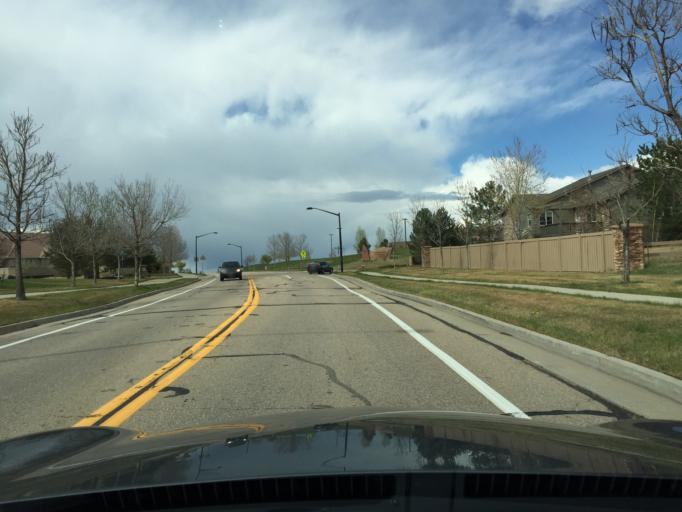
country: US
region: Colorado
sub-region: Boulder County
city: Erie
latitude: 40.0043
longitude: -105.0166
